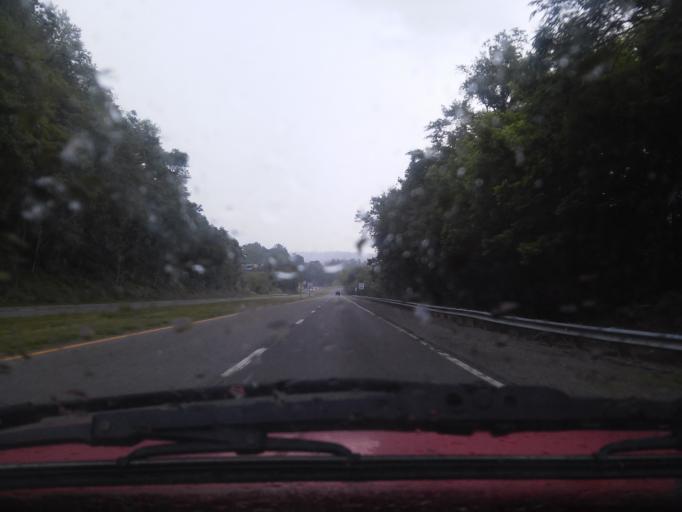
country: US
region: Virginia
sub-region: Montgomery County
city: Prices Fork
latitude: 37.3019
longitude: -80.5060
